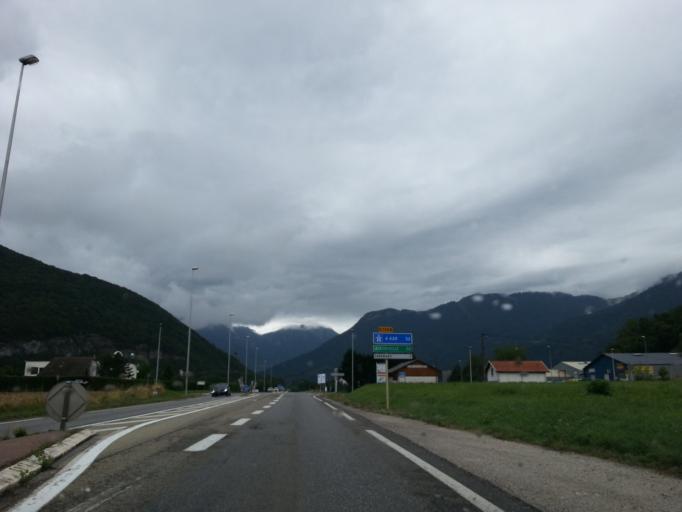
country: FR
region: Rhone-Alpes
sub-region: Departement de la Haute-Savoie
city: Doussard
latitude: 45.7785
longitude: 6.2321
